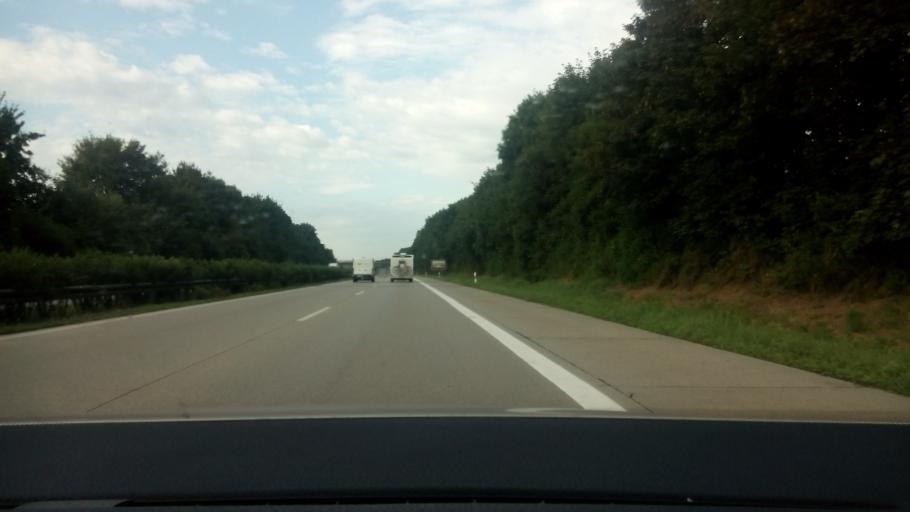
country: DE
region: Bavaria
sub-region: Upper Bavaria
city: Oberschleissheim
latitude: 48.2720
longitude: 11.5427
